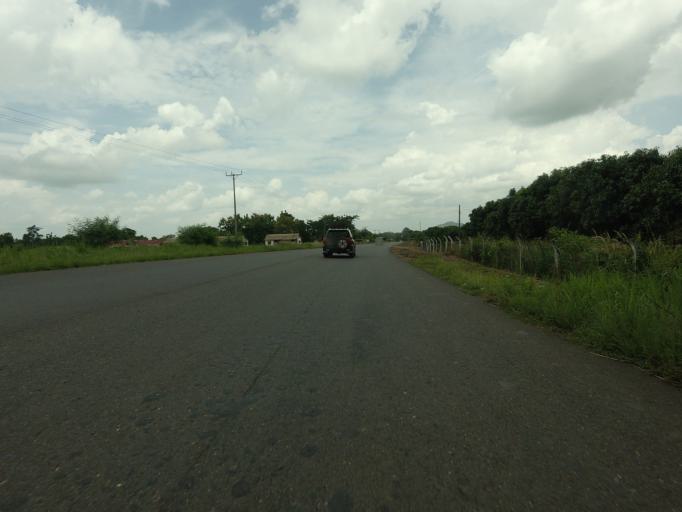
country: GH
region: Volta
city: Ho
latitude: 6.4206
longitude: 0.1720
